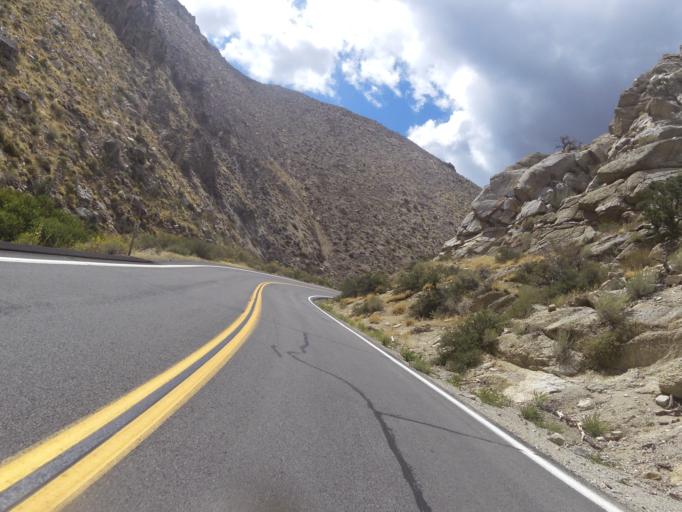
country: US
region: Nevada
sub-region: Lyon County
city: Smith Valley
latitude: 38.6421
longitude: -119.5402
